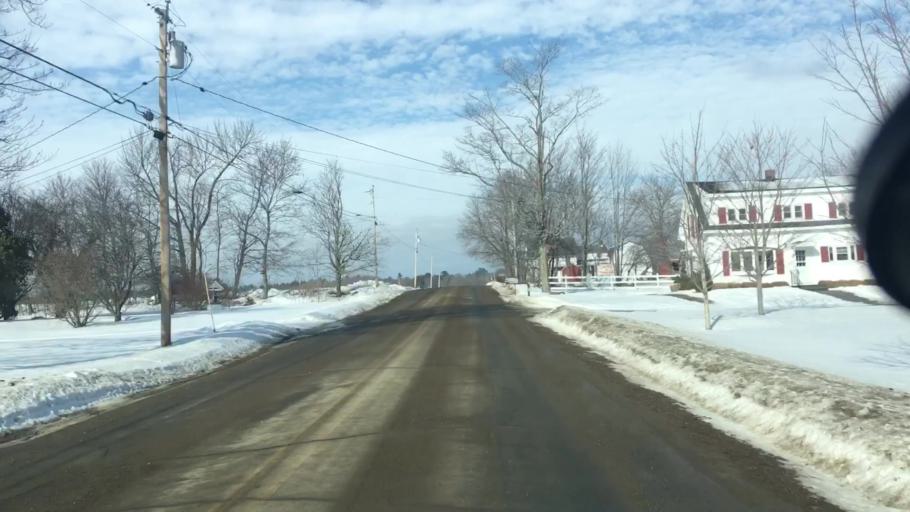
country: US
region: Maine
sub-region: Penobscot County
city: Levant
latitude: 44.8571
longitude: -68.8783
